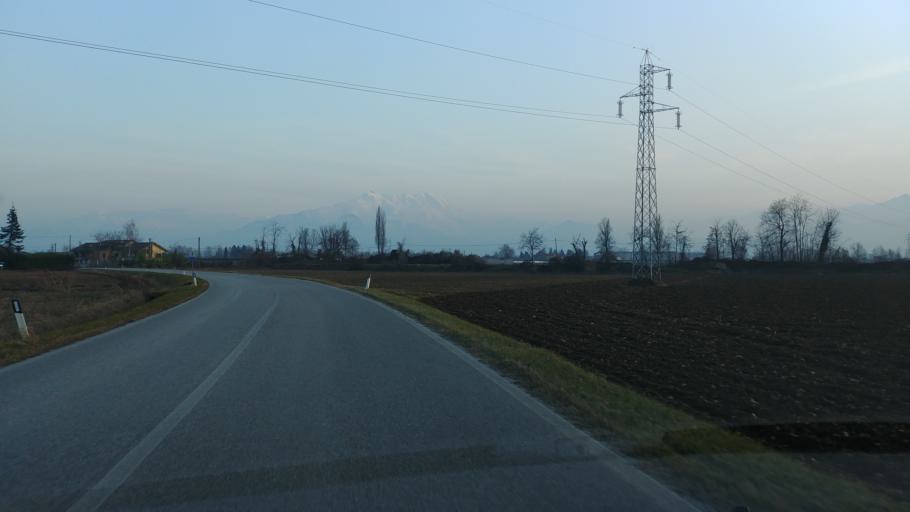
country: IT
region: Piedmont
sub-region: Provincia di Cuneo
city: San Defendente
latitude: 44.4089
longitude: 7.5166
